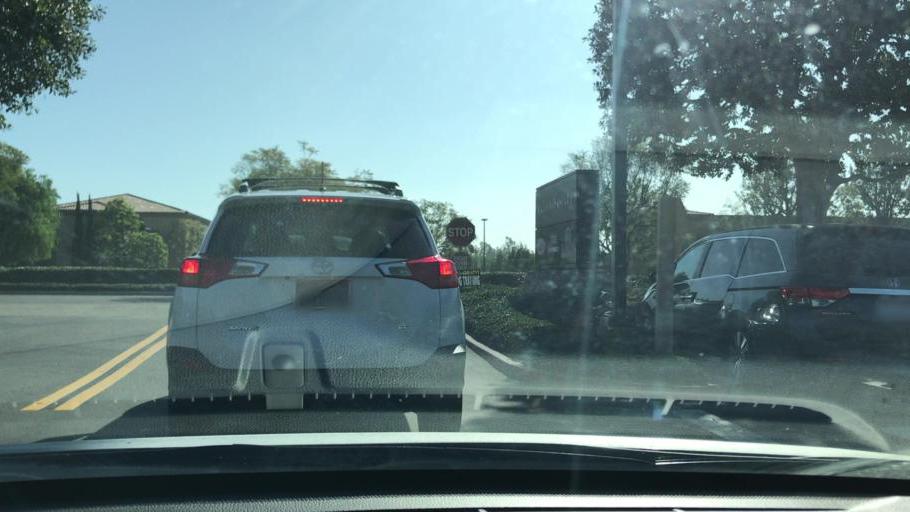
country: US
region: California
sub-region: Orange County
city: Irvine
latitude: 33.6707
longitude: -117.7882
